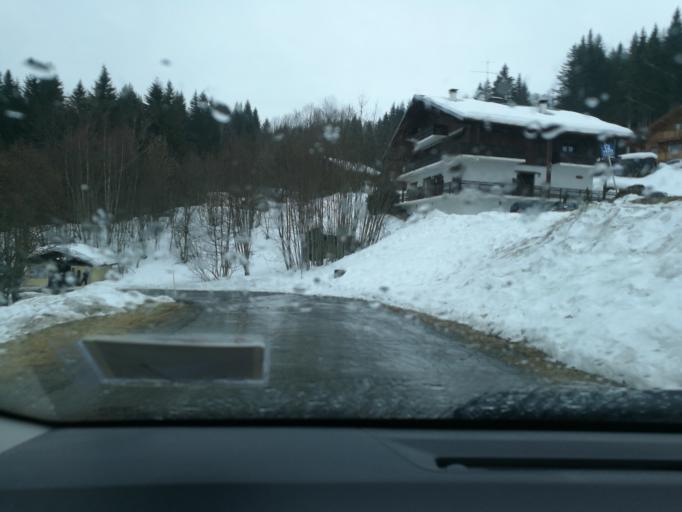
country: FR
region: Rhone-Alpes
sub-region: Departement de la Haute-Savoie
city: Saint-Gervais-les-Bains
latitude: 45.8651
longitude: 6.6928
